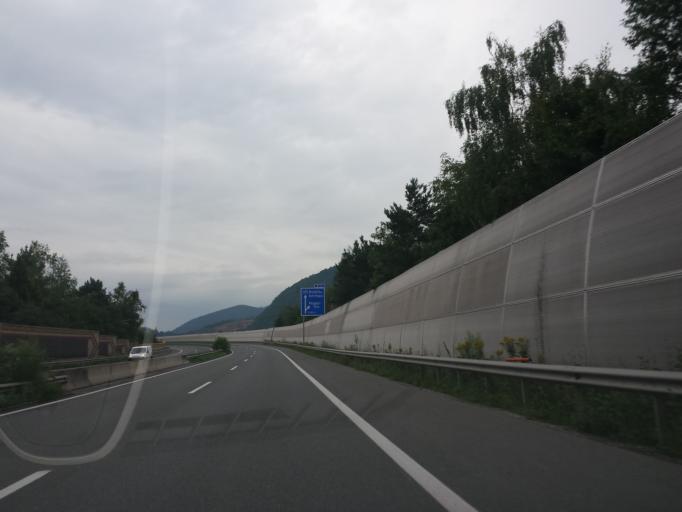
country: AT
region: Styria
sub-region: Politischer Bezirk Graz-Umgebung
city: Peggau
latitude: 47.1982
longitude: 15.3455
